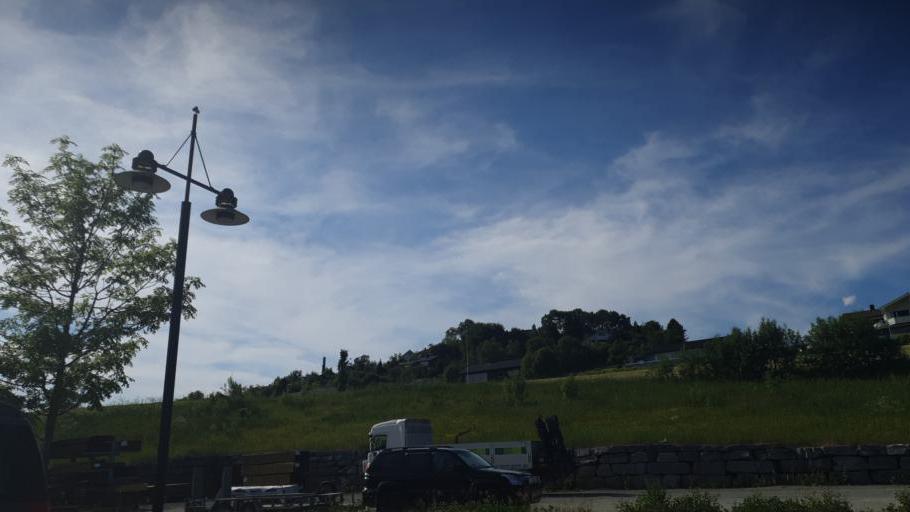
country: NO
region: Nord-Trondelag
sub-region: Leksvik
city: Leksvik
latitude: 63.6733
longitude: 10.6253
